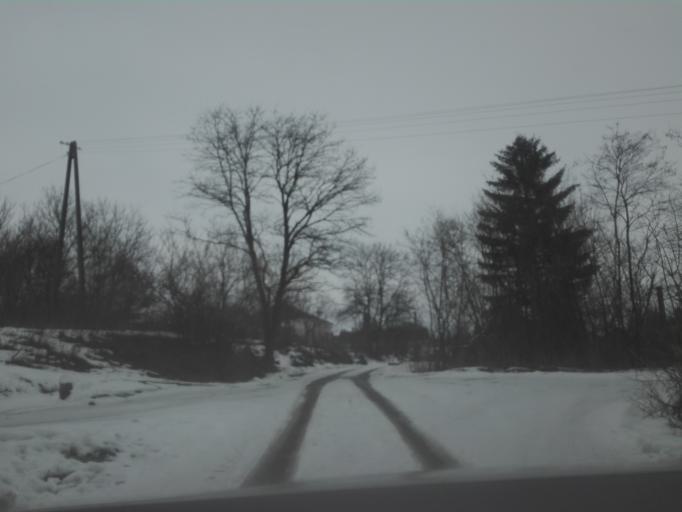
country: PL
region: Lublin Voivodeship
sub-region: Powiat hrubieszowski
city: Horodlo
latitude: 50.8483
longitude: 24.0288
